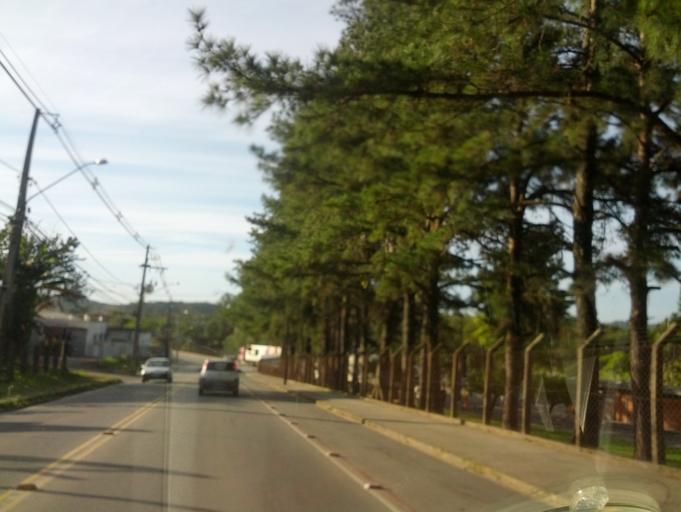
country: BR
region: Santa Catarina
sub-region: Indaial
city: Indaial
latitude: -26.9061
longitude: -49.1494
